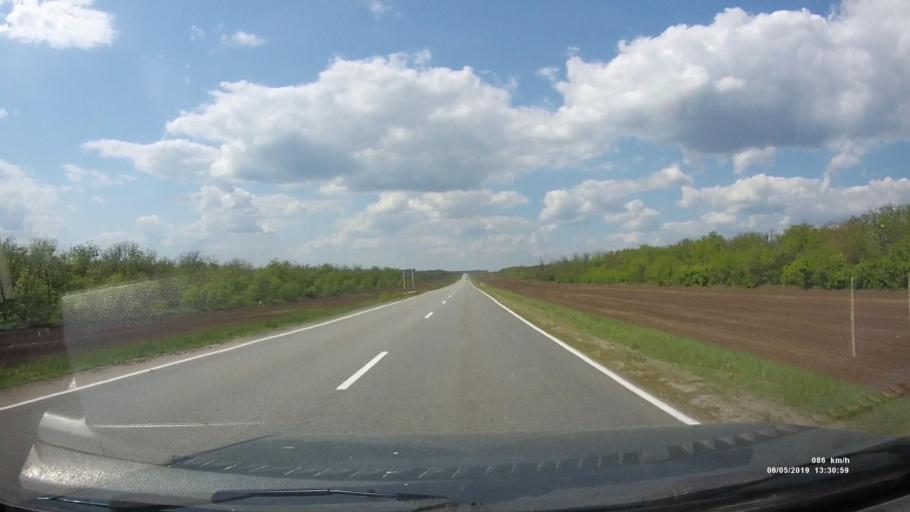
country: RU
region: Rostov
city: Ust'-Donetskiy
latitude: 47.6733
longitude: 40.8175
